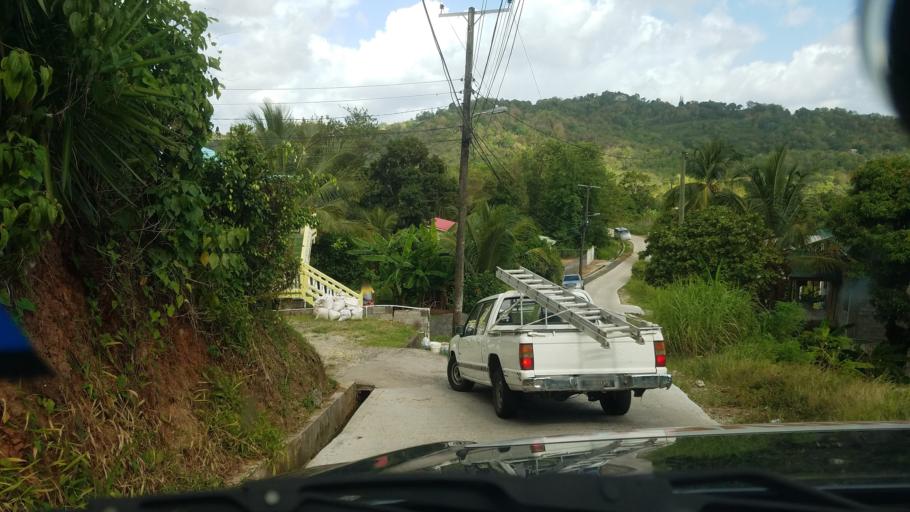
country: LC
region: Castries Quarter
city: Bisee
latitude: 14.0073
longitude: -60.9553
